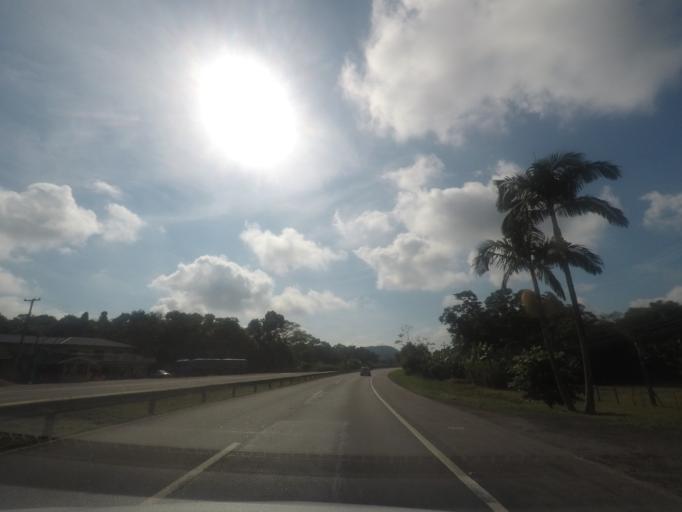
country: BR
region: Parana
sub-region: Antonina
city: Antonina
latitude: -25.5400
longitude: -48.7752
